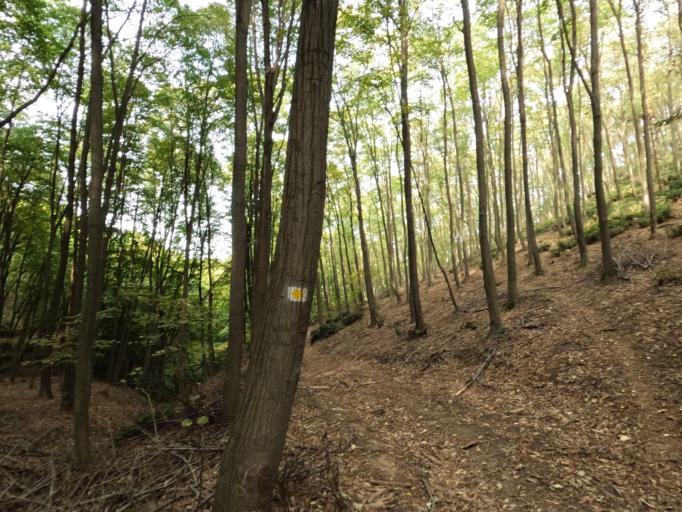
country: HU
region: Tolna
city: Szekszard
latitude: 46.3144
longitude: 18.6616
